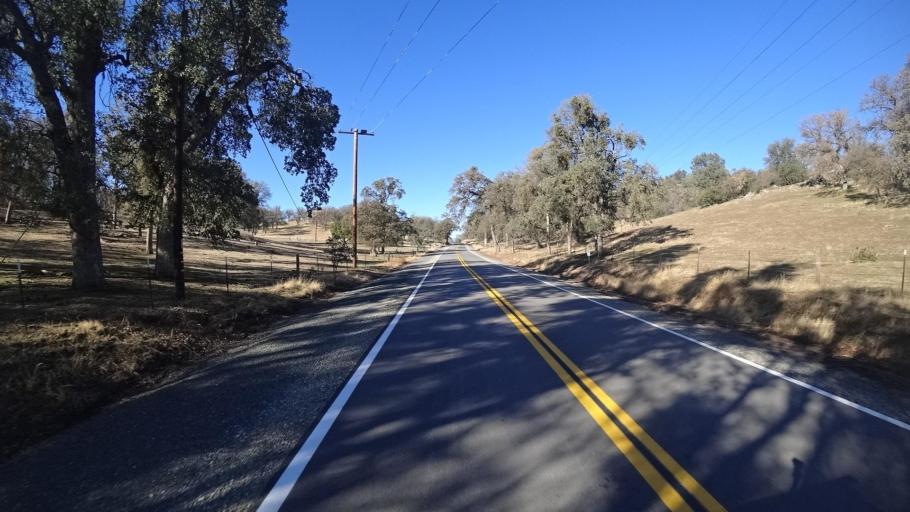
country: US
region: California
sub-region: Kern County
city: Alta Sierra
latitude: 35.7053
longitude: -118.7495
